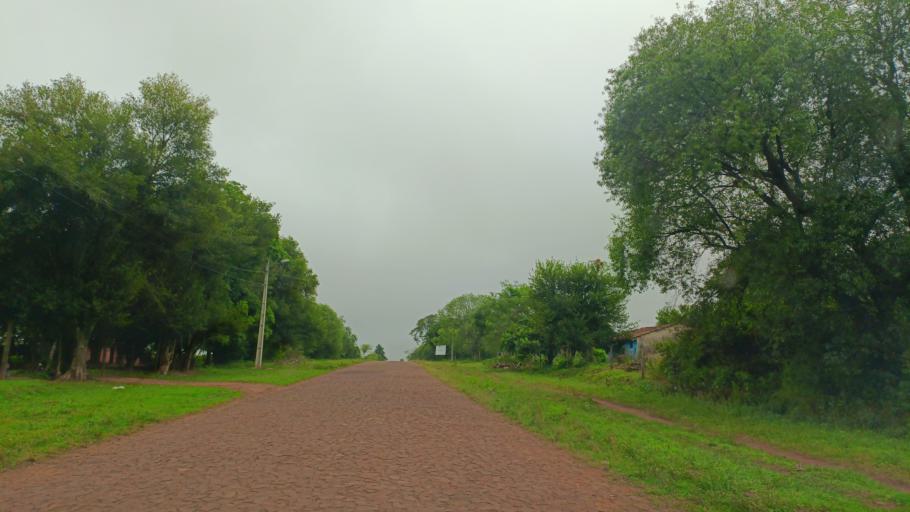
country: PY
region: Misiones
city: Santa Maria
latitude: -26.8781
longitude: -57.0128
